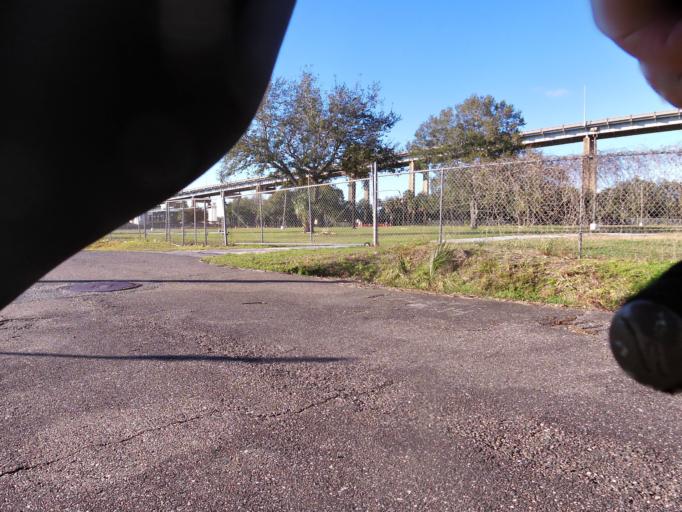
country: US
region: Florida
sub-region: Duval County
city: Jacksonville
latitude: 30.3256
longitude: -81.6283
